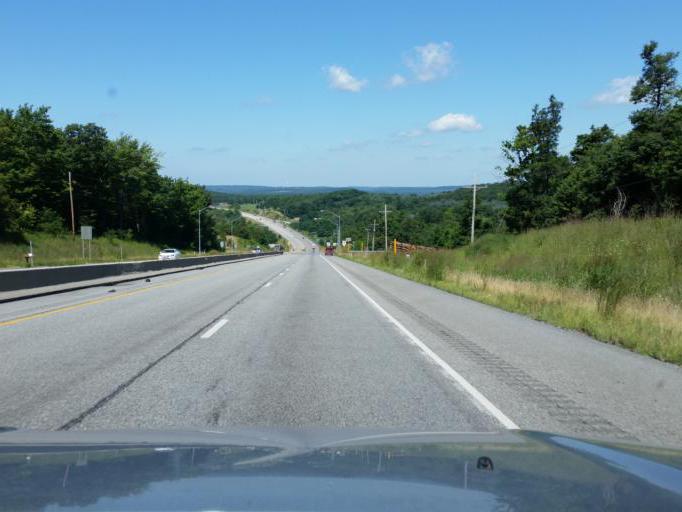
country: US
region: Pennsylvania
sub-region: Cambria County
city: Vinco
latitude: 40.4383
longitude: -78.9316
